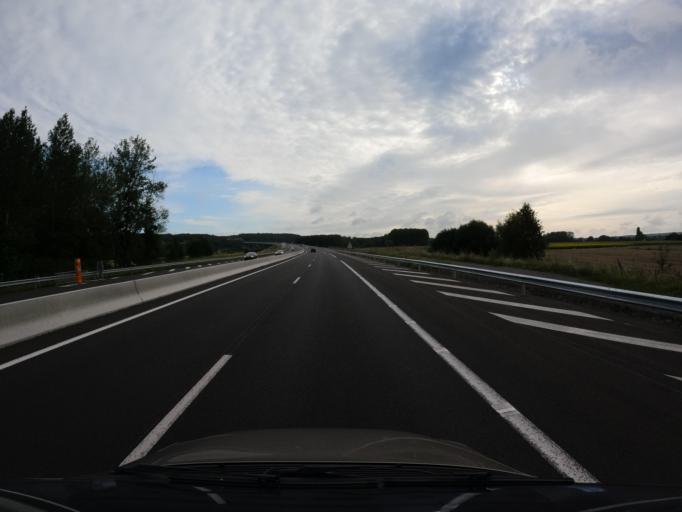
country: FR
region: Centre
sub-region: Departement d'Indre-et-Loire
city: Restigne
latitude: 47.2771
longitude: 0.2729
